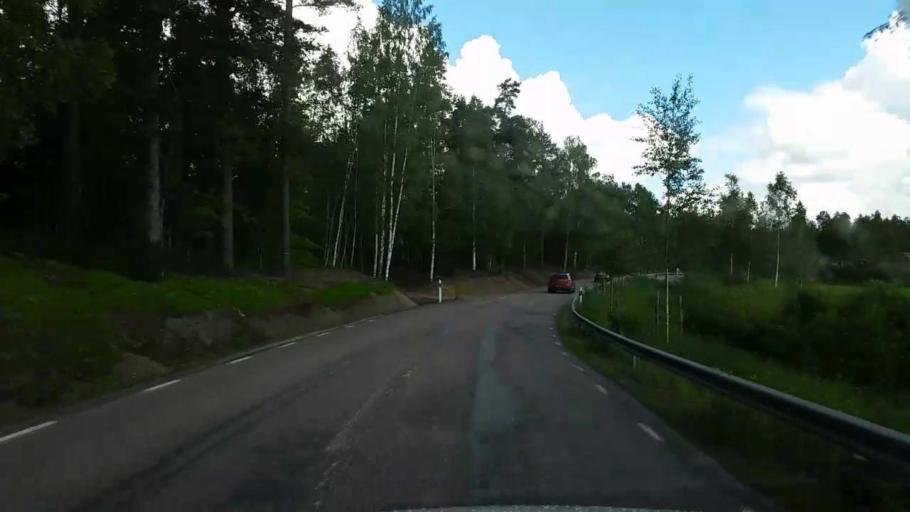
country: SE
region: Vaestmanland
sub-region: Skinnskattebergs Kommun
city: Skinnskatteberg
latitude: 59.8546
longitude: 15.8423
